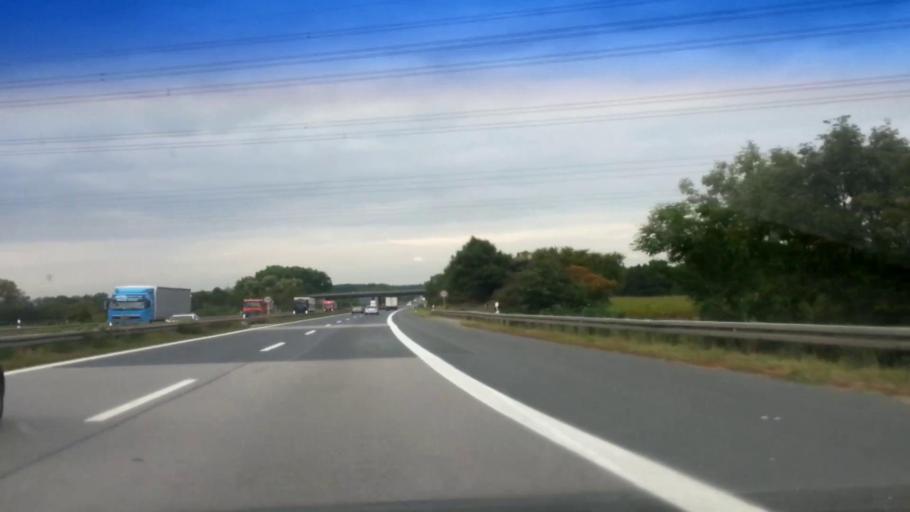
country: DE
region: Bavaria
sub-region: Upper Franconia
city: Gundelsheim
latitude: 49.9329
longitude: 10.9133
